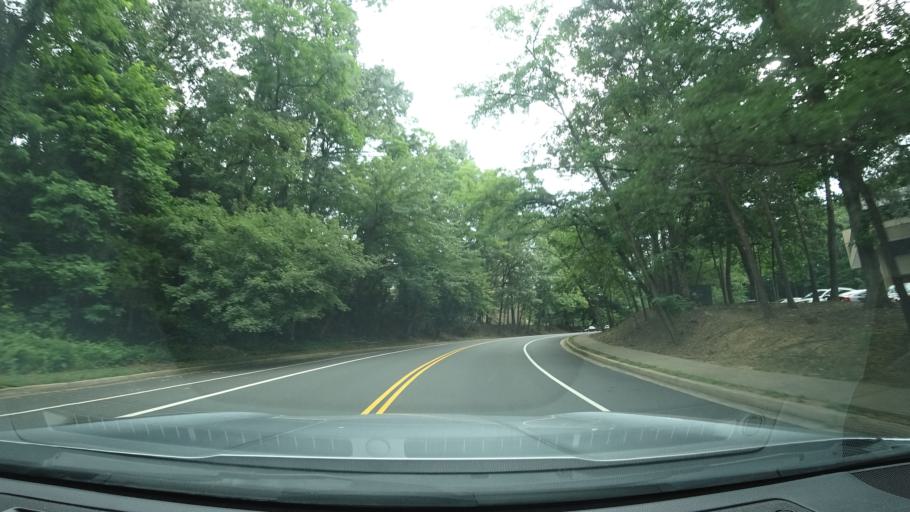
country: US
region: Virginia
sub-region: Fairfax County
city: Reston
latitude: 38.9685
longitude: -77.3435
